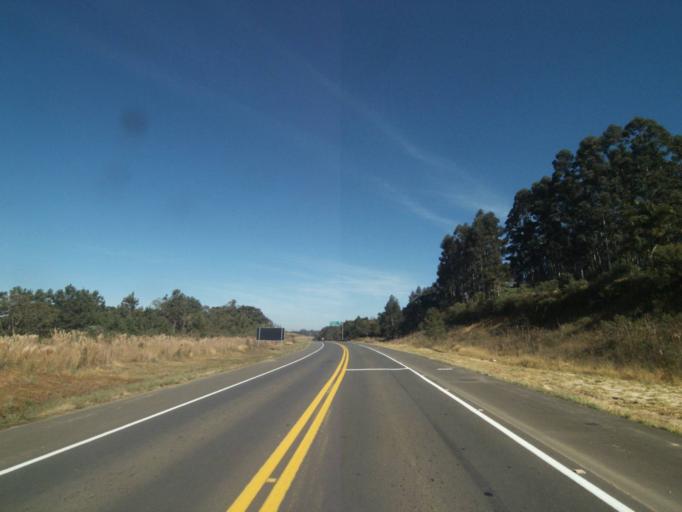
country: BR
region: Parana
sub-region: Tibagi
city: Tibagi
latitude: -24.8102
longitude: -50.4818
